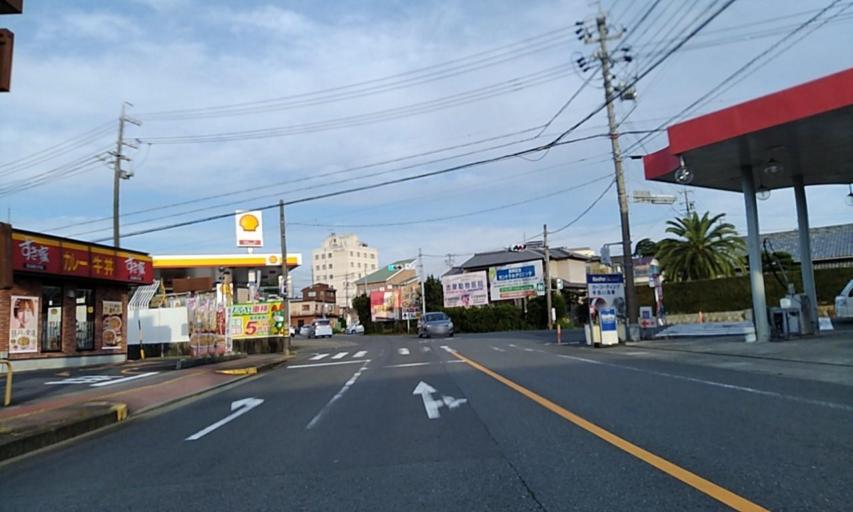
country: JP
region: Mie
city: Toba
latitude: 34.3295
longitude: 136.8211
